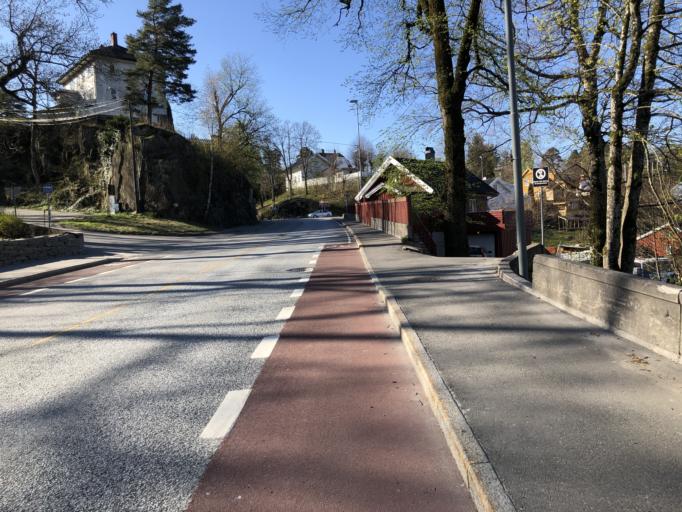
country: NO
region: Aust-Agder
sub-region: Arendal
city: Arendal
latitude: 58.4697
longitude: 8.7585
